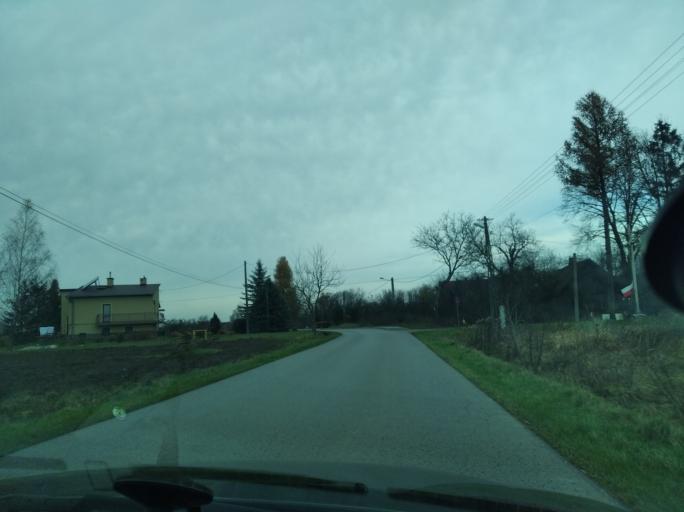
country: PL
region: Subcarpathian Voivodeship
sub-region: Powiat lancucki
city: Rogozno
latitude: 50.0975
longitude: 22.4052
